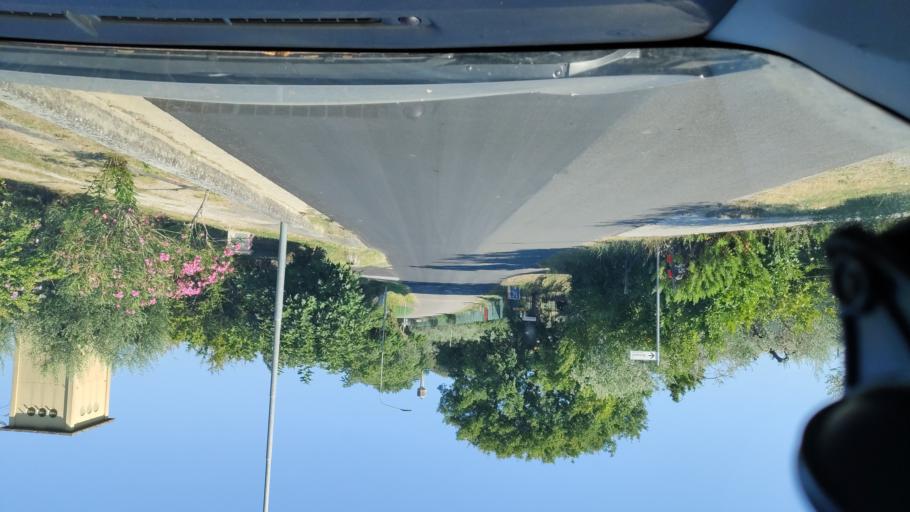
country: IT
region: Umbria
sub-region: Provincia di Terni
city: Fornole
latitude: 42.5169
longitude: 12.4314
